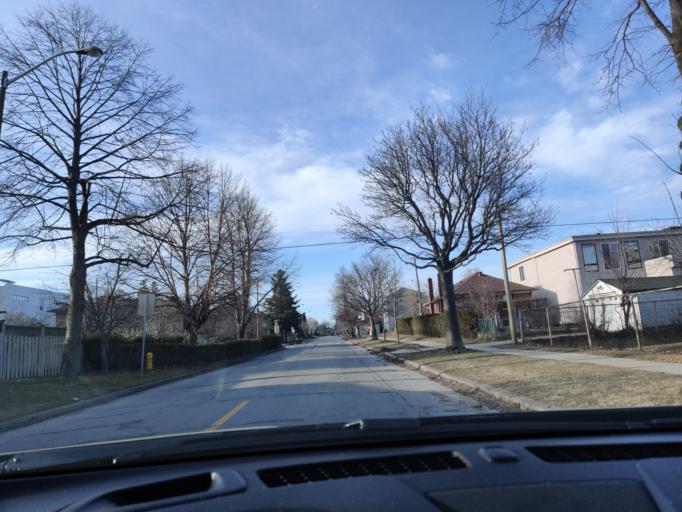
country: CA
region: Ontario
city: Toronto
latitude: 43.7069
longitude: -79.4461
